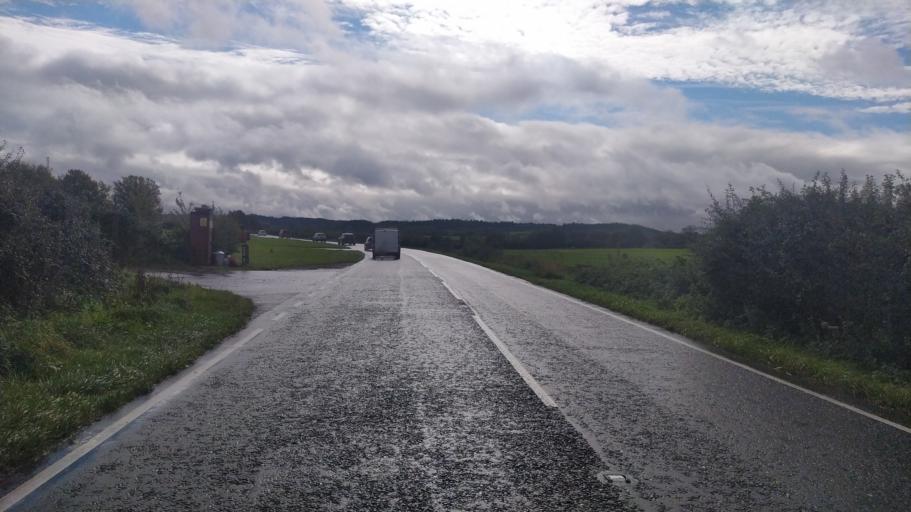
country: GB
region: England
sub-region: Dorset
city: Lytchett Matravers
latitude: 50.8032
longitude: -2.0906
